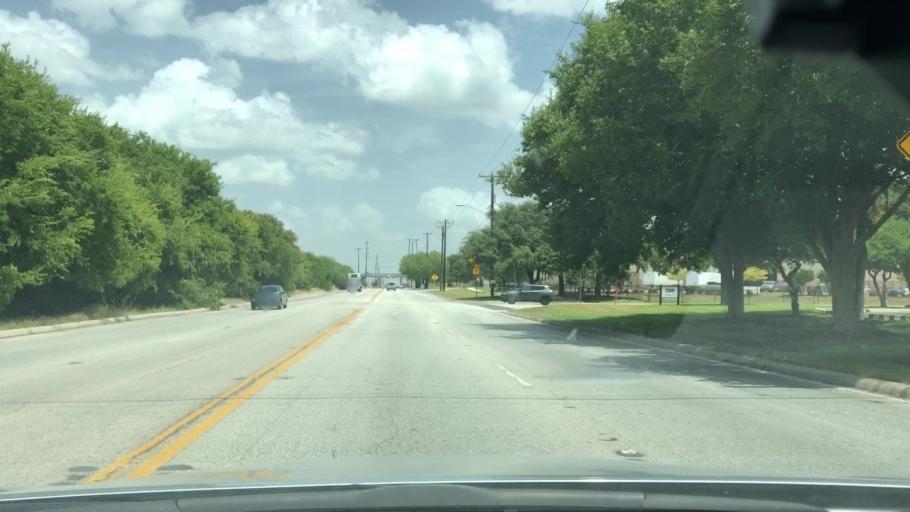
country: US
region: Texas
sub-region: Bexar County
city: Kirby
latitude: 29.4570
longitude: -98.4082
